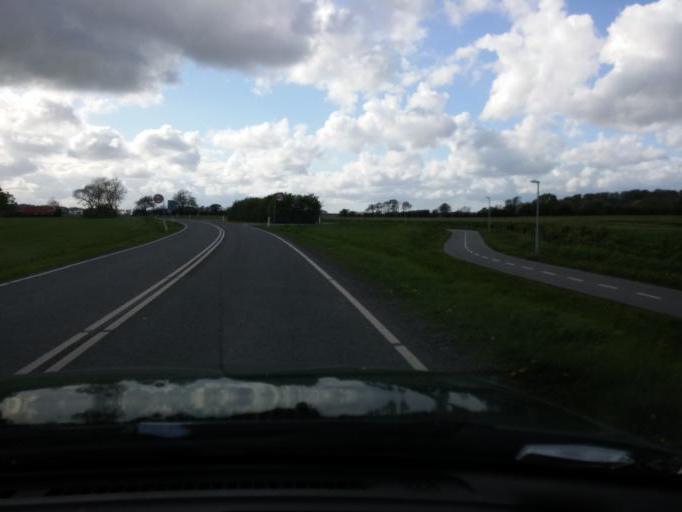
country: DK
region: South Denmark
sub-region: Faaborg-Midtfyn Kommune
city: Ringe
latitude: 55.2446
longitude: 10.5287
